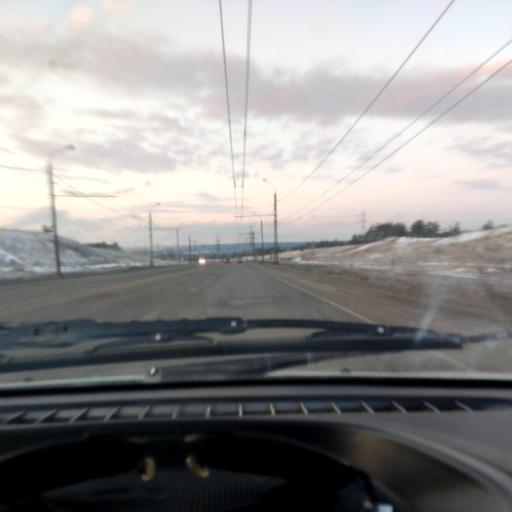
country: RU
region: Samara
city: Zhigulevsk
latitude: 53.5117
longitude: 49.5261
